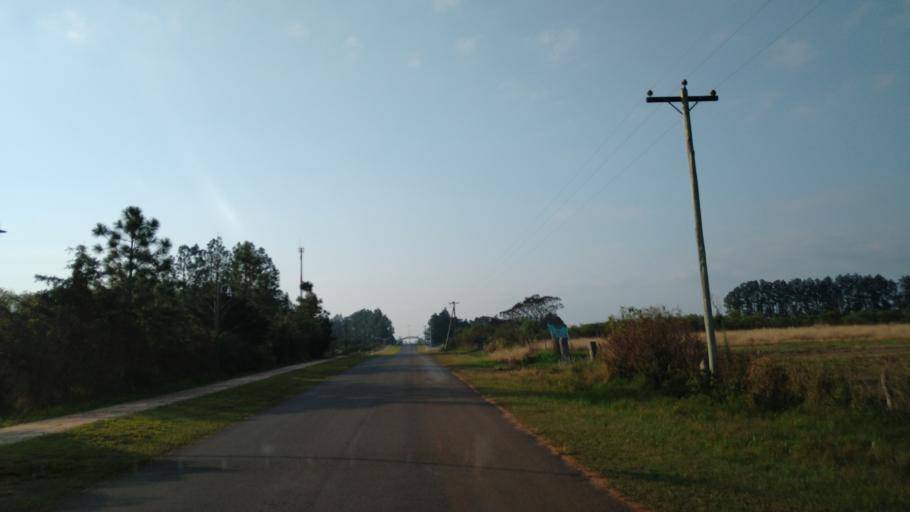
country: AR
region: Entre Rios
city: Santa Ana
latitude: -30.9038
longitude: -57.9249
